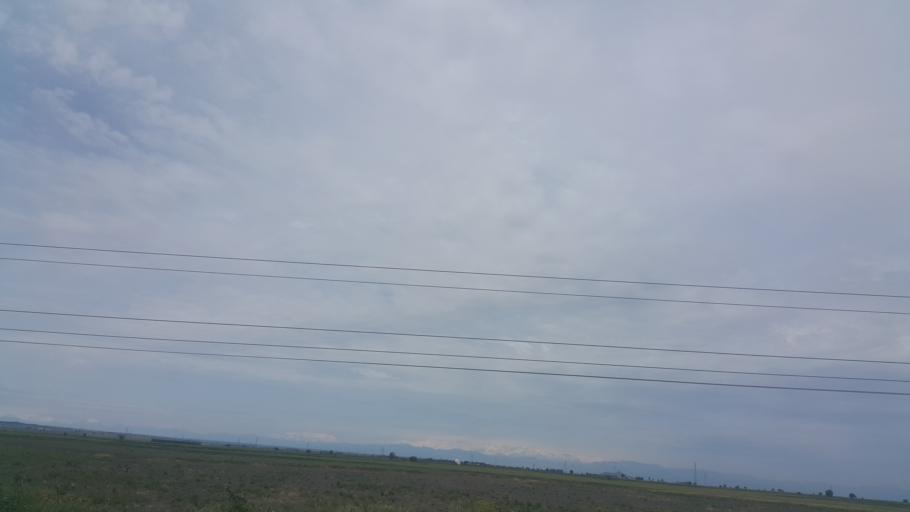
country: TR
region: Adana
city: Ceyhan
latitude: 37.0413
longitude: 35.7579
